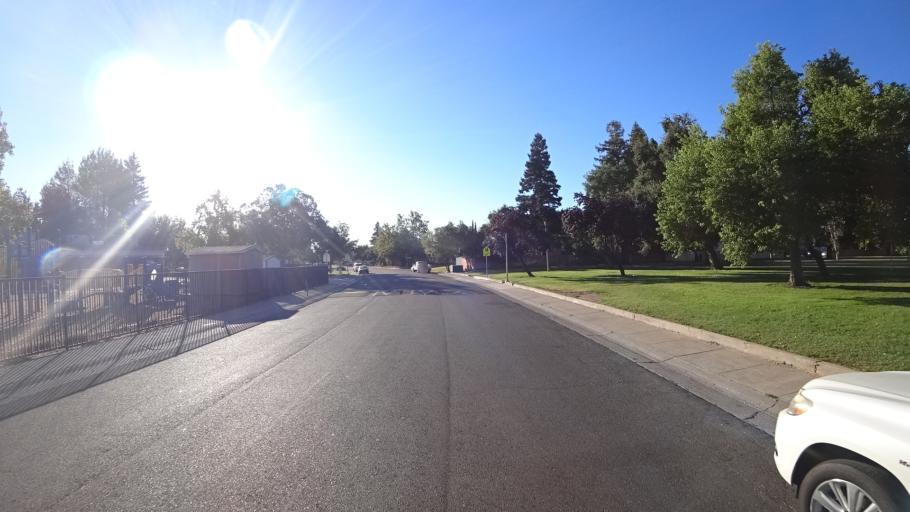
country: US
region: California
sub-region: Sacramento County
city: Florin
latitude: 38.4632
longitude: -121.4237
